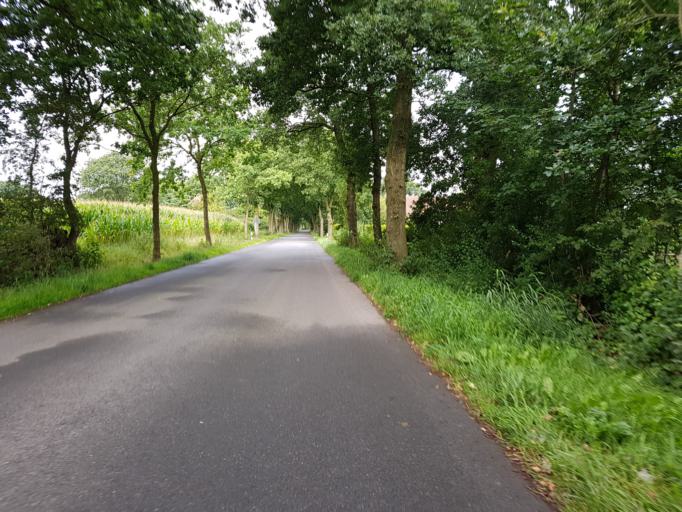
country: DE
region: Lower Saxony
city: Wittmund
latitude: 53.5518
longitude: 7.8065
